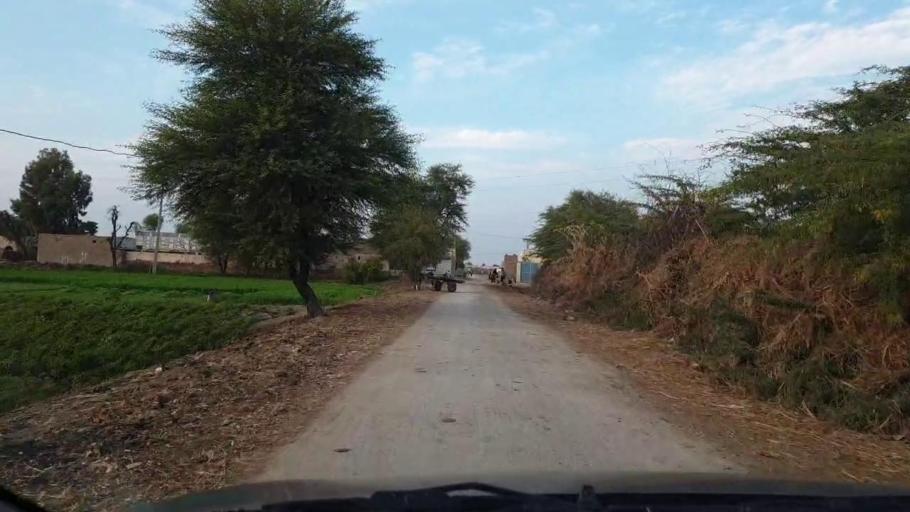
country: PK
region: Sindh
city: Jhol
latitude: 25.9848
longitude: 68.8656
